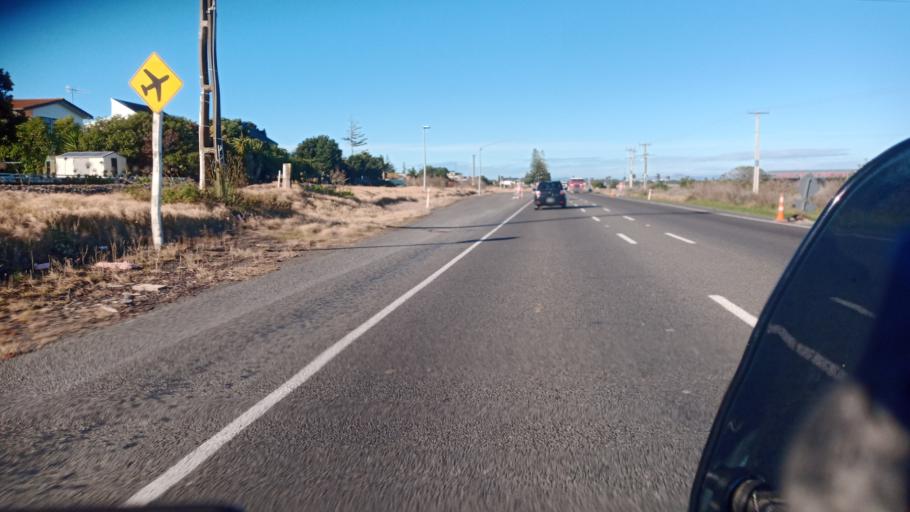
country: NZ
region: Hawke's Bay
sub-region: Napier City
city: Napier
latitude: -39.4618
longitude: 176.8733
